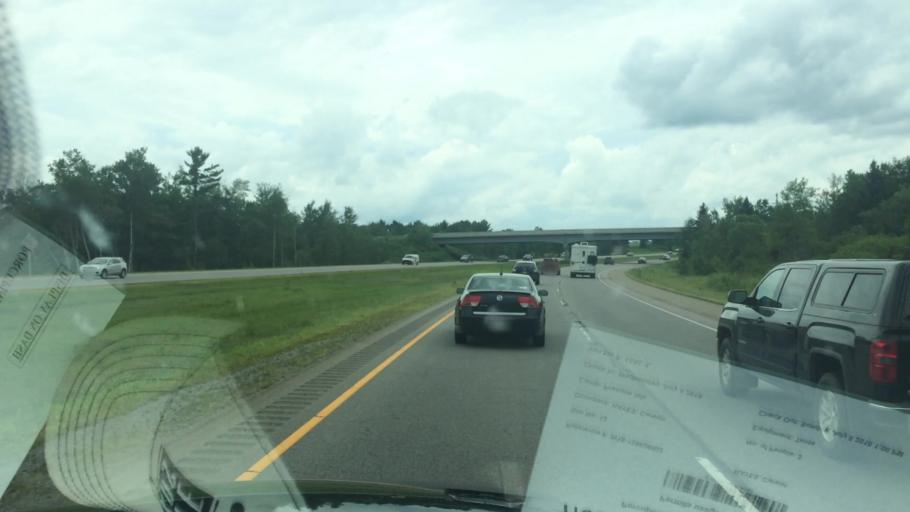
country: US
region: Wisconsin
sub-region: Marathon County
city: Mosinee
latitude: 44.7272
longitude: -89.6767
